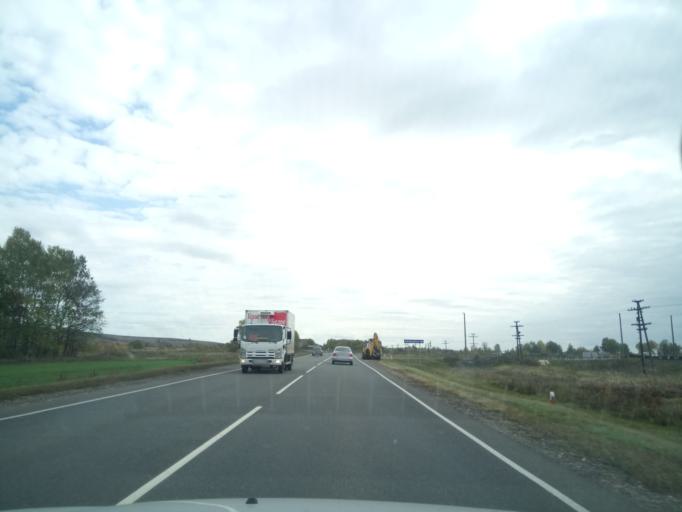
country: RU
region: Nizjnij Novgorod
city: Lukoyanov
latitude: 55.0691
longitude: 44.3436
